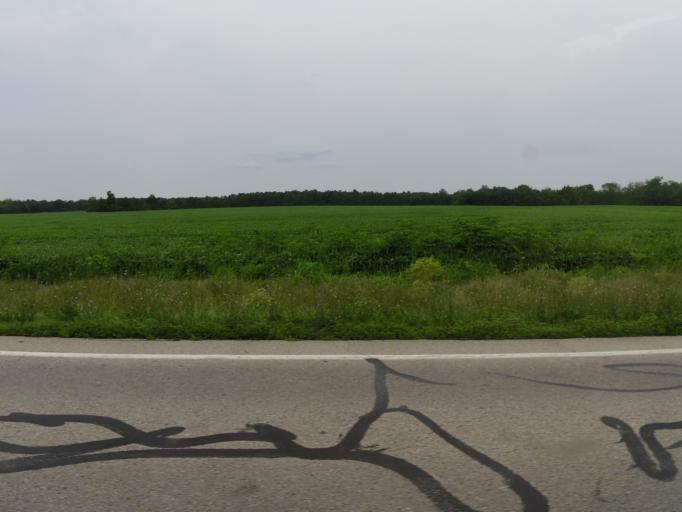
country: US
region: Ohio
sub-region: Warren County
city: Waynesville
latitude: 39.4930
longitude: -83.9663
